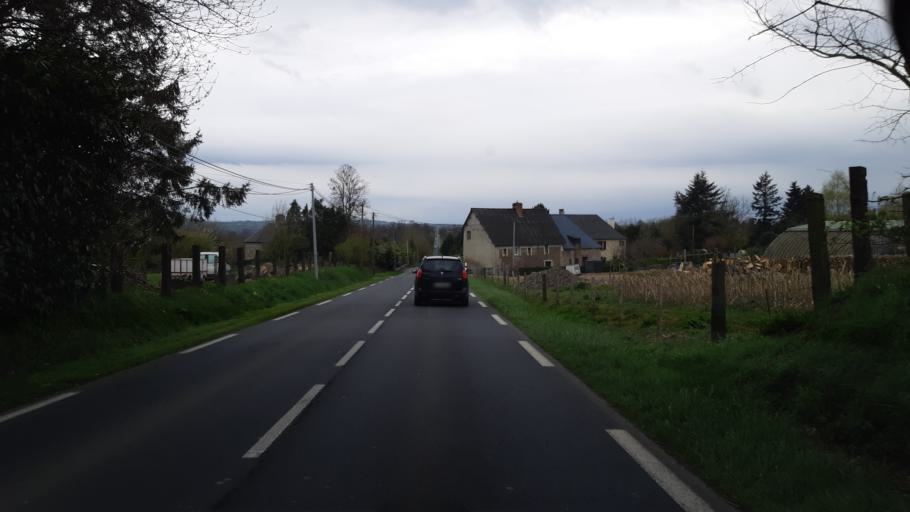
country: FR
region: Lower Normandy
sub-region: Departement de la Manche
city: Tessy-sur-Vire
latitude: 49.0261
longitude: -1.1452
